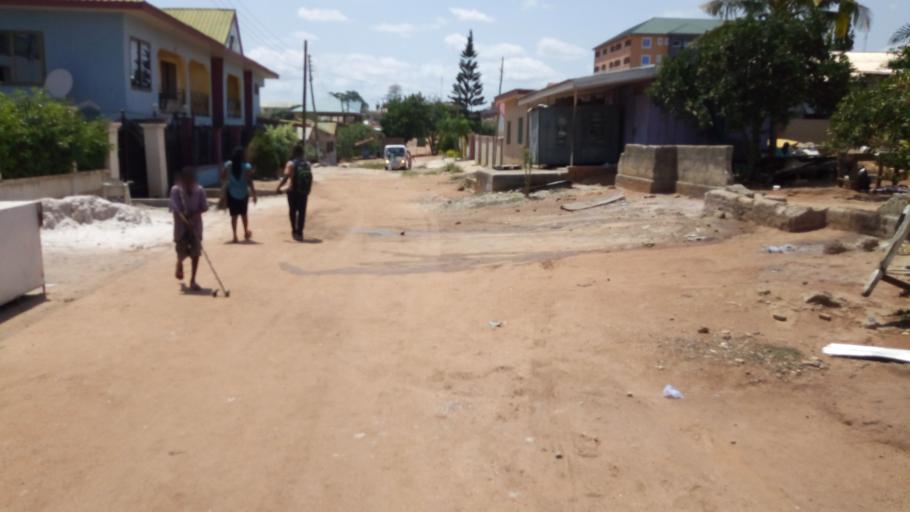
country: GH
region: Ashanti
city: Mamponteng
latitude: 6.6744
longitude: -1.5603
